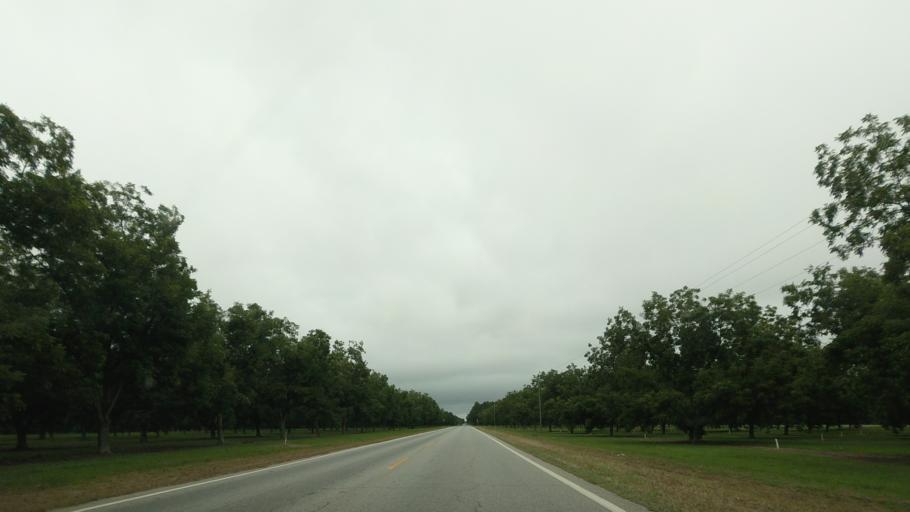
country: US
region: Georgia
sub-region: Berrien County
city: Ray City
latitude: 31.0939
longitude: -83.2064
